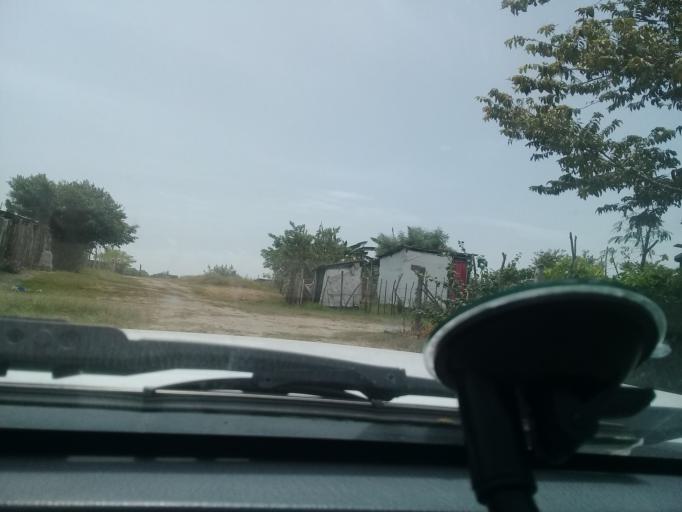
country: MX
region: Veracruz
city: Anahuac
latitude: 22.2250
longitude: -97.8271
